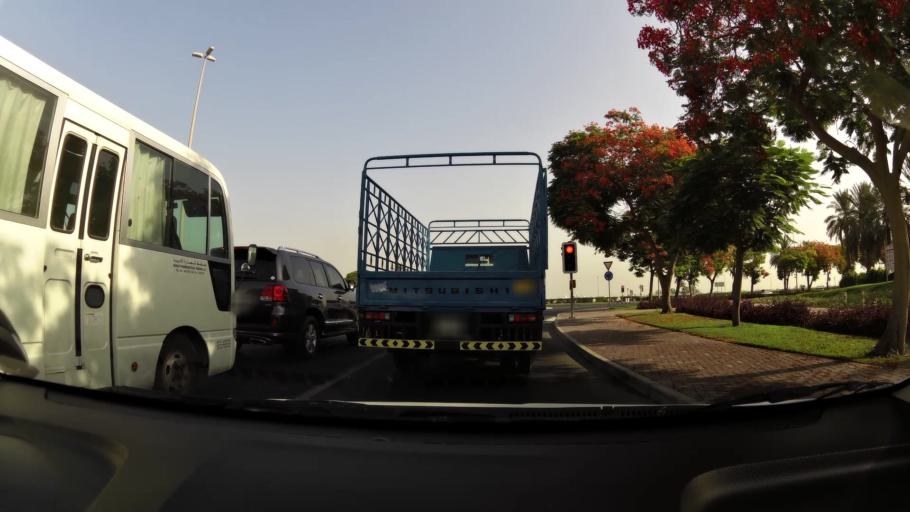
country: AE
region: Ash Shariqah
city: Sharjah
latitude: 25.2793
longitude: 55.3106
